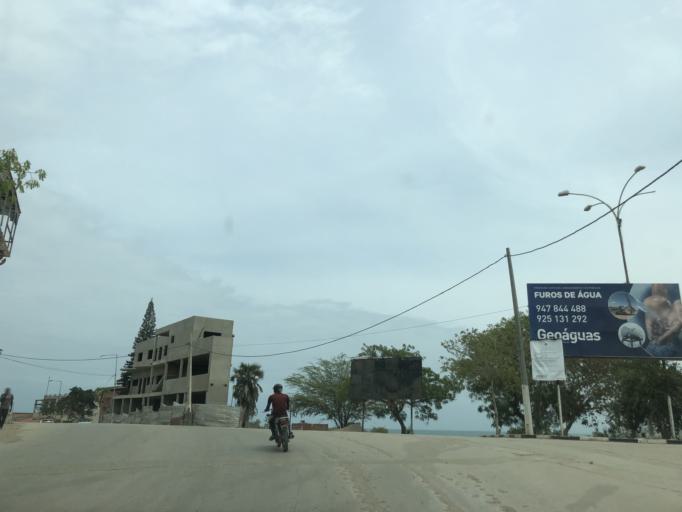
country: AO
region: Cuanza Sul
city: Sumbe
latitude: -11.1964
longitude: 13.8381
